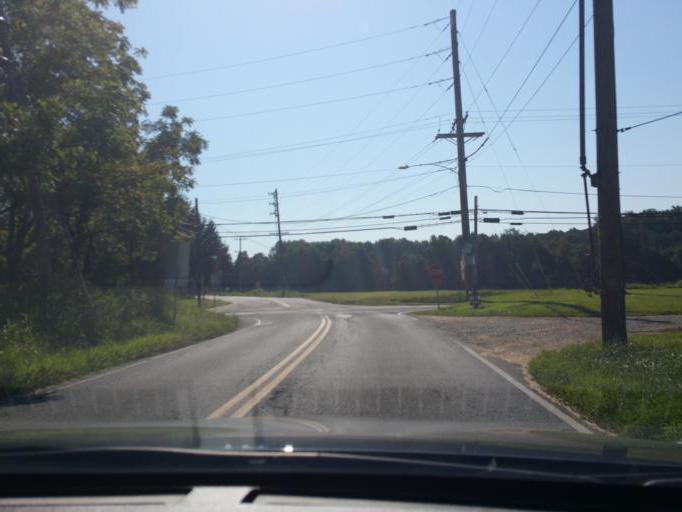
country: US
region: Maryland
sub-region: Cecil County
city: Rising Sun
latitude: 39.6415
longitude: -76.1268
